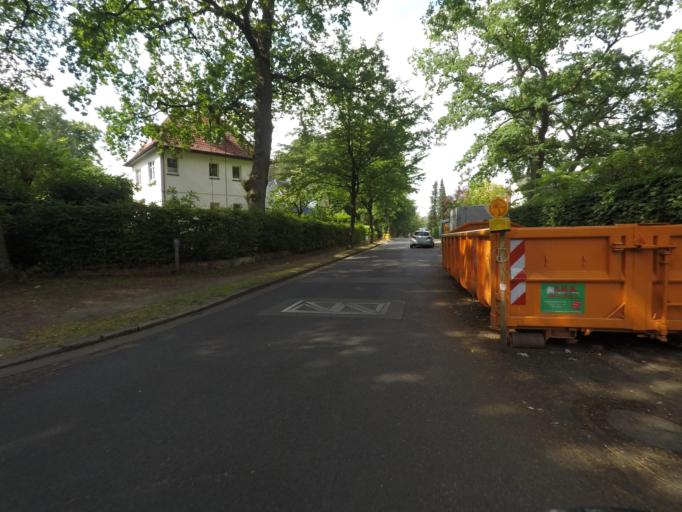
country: DE
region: Hamburg
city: Wellingsbuettel
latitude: 53.6360
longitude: 10.0652
